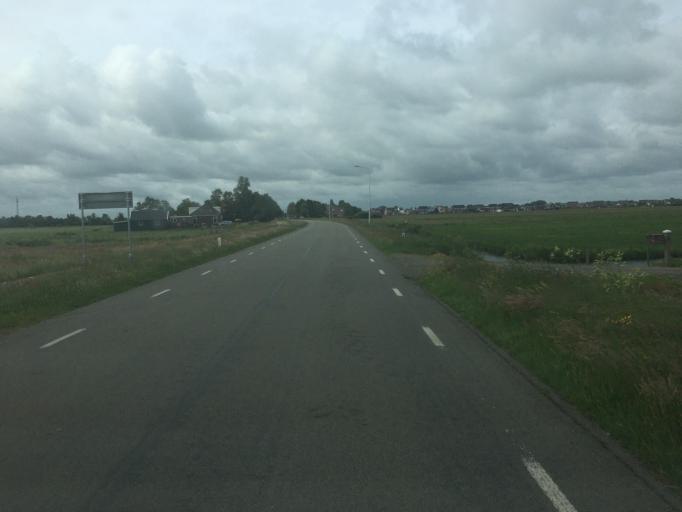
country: NL
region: Friesland
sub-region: Gemeente Lemsterland
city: Echtenerbrug
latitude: 52.8795
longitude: 5.8313
